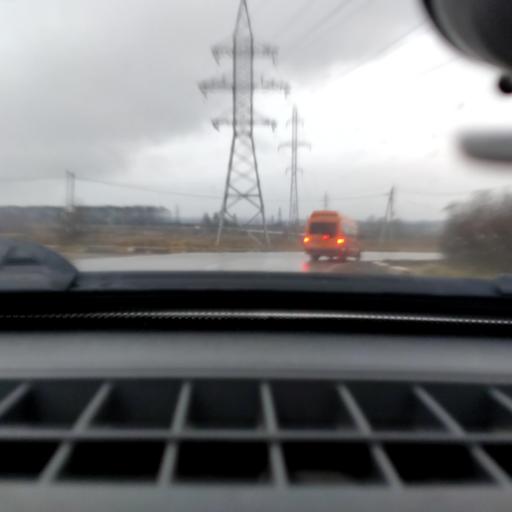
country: RU
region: Bashkortostan
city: Iglino
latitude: 54.7542
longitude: 56.2542
